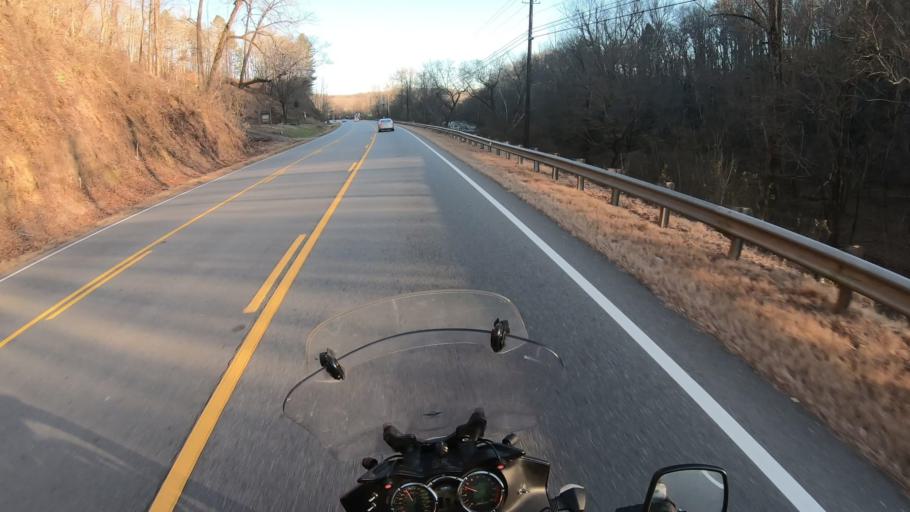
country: US
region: Georgia
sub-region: Lumpkin County
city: Dahlonega
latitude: 34.4718
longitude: -83.9739
